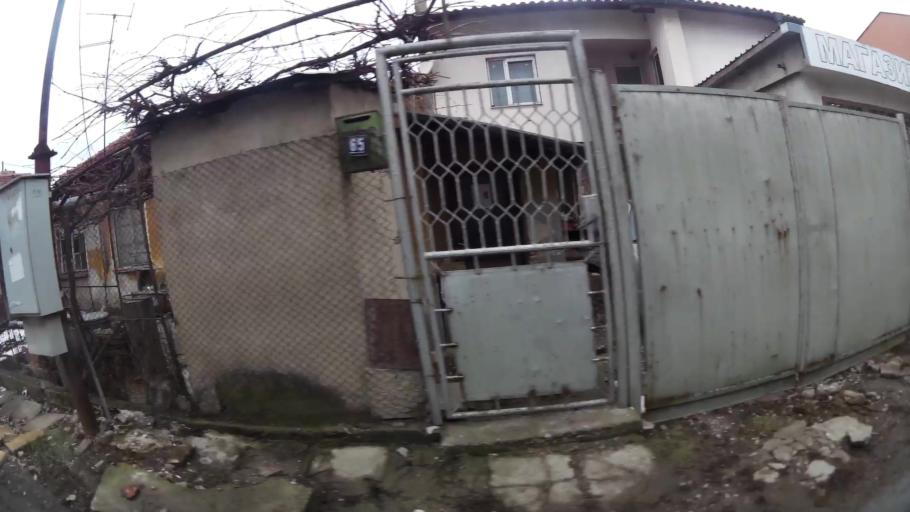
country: BG
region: Sofia-Capital
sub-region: Stolichna Obshtina
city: Sofia
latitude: 42.7274
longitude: 23.2814
